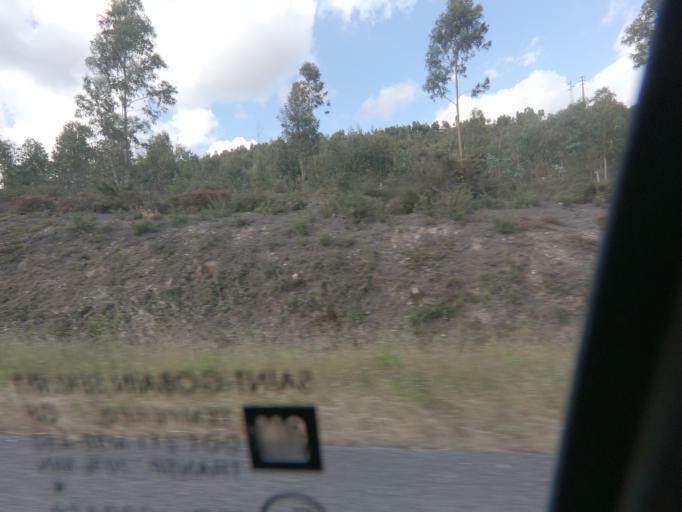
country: PT
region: Porto
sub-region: Valongo
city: Campo
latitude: 41.1895
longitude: -8.4791
